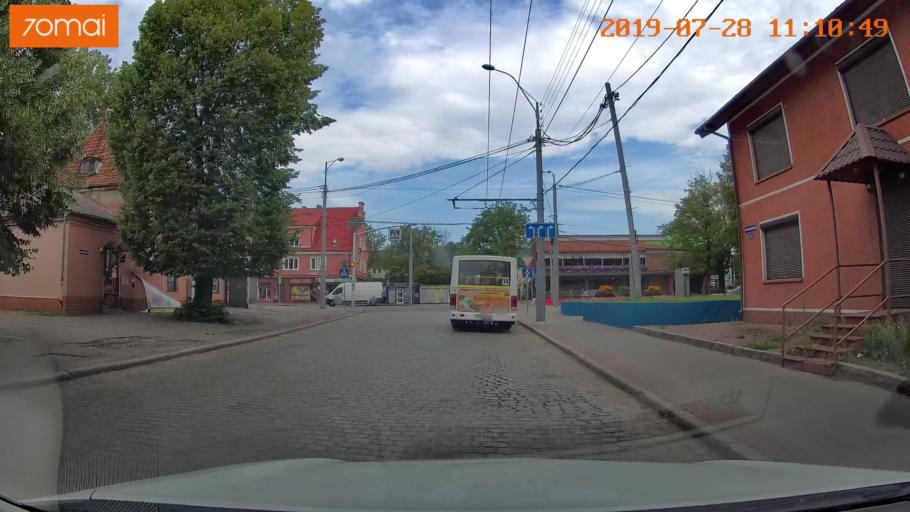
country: RU
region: Kaliningrad
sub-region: Gorod Kaliningrad
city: Kaliningrad
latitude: 54.7137
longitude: 20.4584
